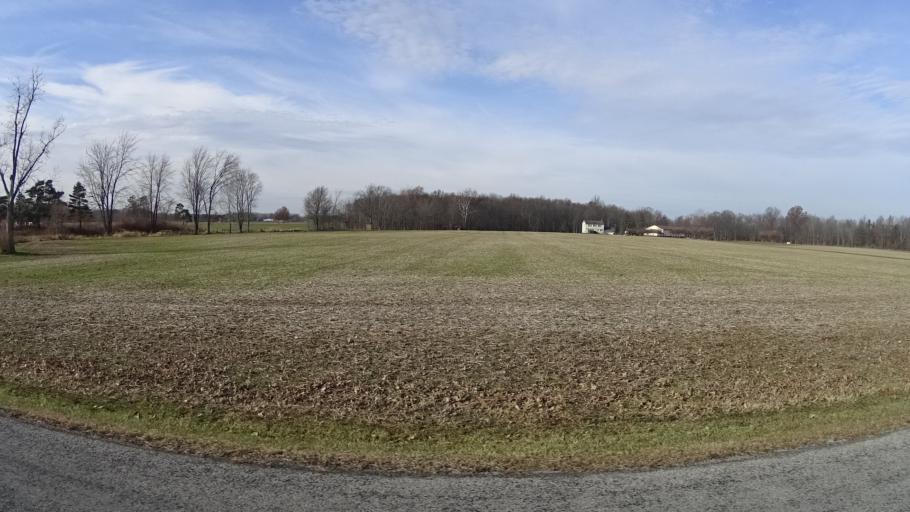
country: US
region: Ohio
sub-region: Lorain County
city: Grafton
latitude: 41.2132
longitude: -82.0628
